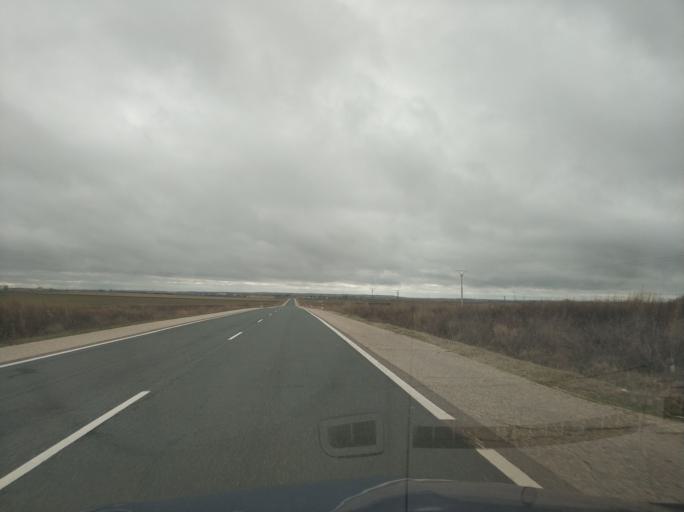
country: ES
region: Castille and Leon
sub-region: Provincia de Salamanca
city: Pajares de la Laguna
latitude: 41.0806
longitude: -5.5210
